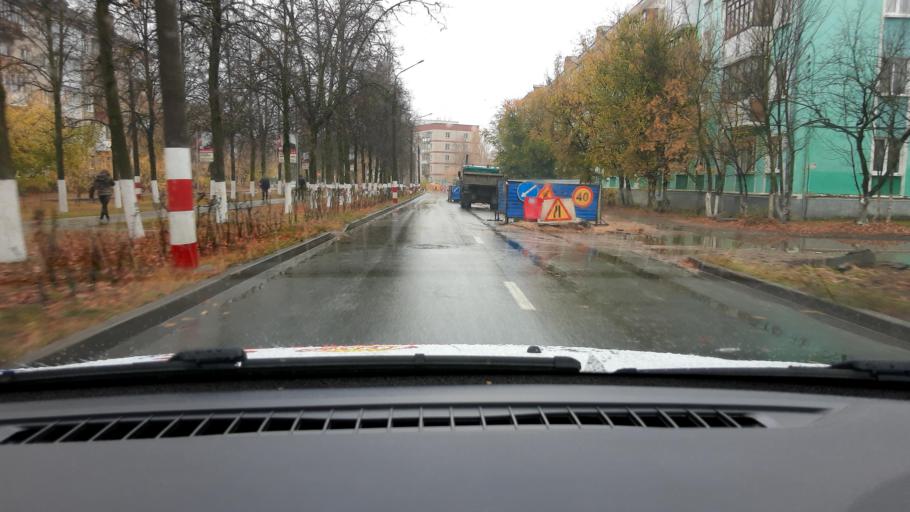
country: RU
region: Nizjnij Novgorod
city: Dzerzhinsk
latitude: 56.2408
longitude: 43.4444
